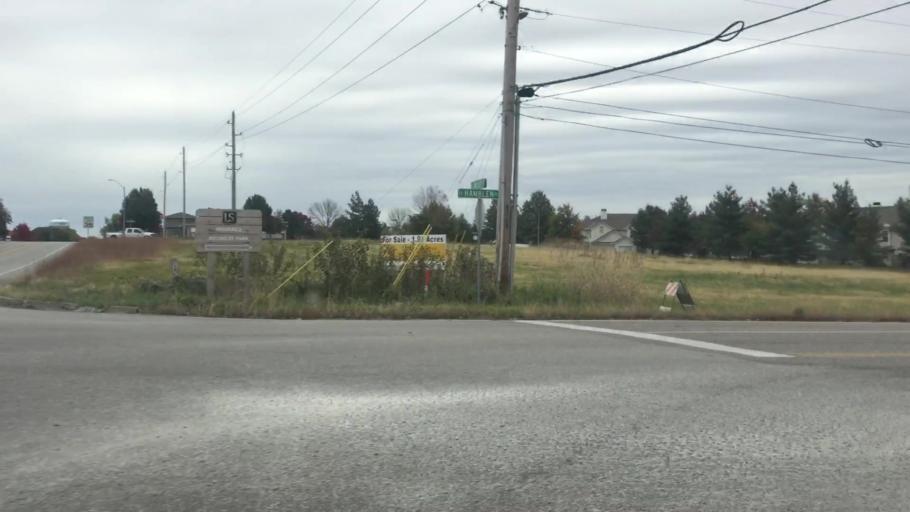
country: US
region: Missouri
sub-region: Jackson County
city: Lees Summit
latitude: 38.8956
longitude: -94.3590
